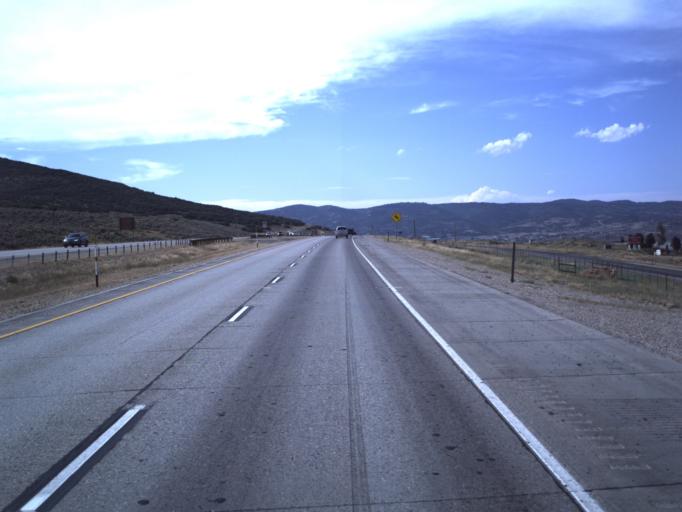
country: US
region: Utah
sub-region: Summit County
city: Park City
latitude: 40.6923
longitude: -111.4684
